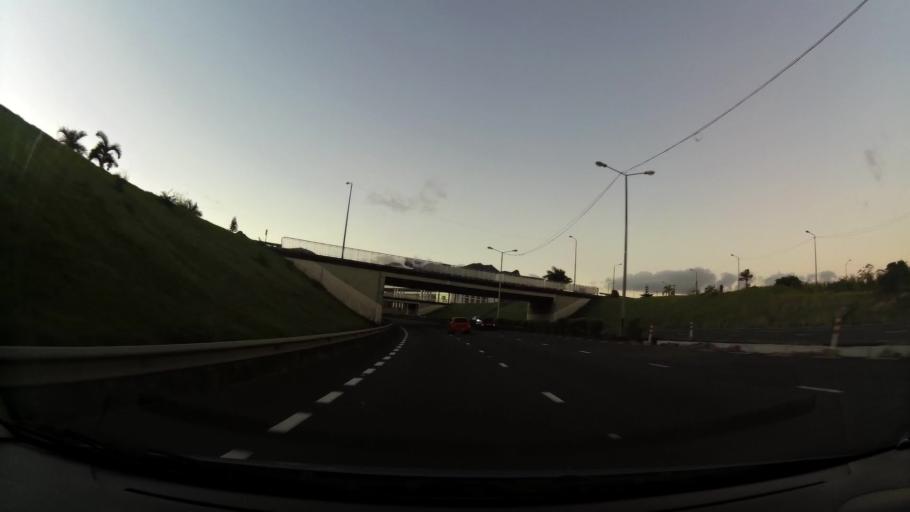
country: MU
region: Moka
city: Moka
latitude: -20.2324
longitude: 57.5007
